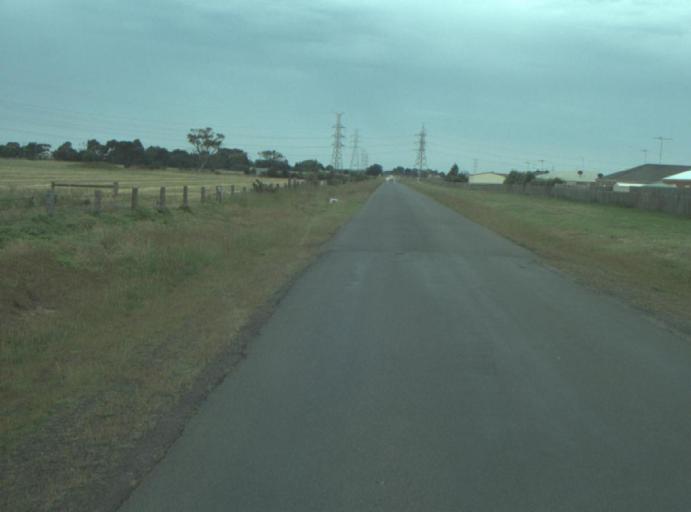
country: AU
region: Victoria
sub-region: Greater Geelong
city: Breakwater
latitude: -38.1916
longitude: 144.3992
